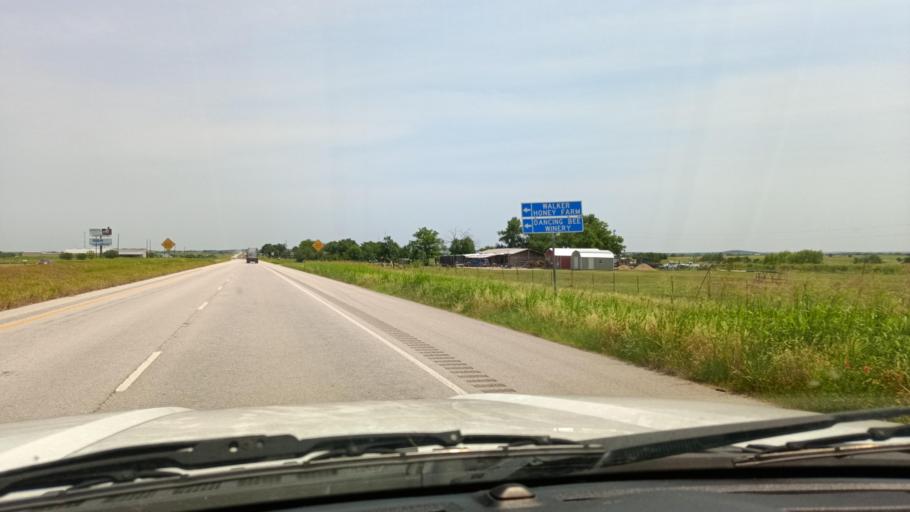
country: US
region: Texas
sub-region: Bell County
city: Little River-Academy
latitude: 30.9986
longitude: -97.2887
